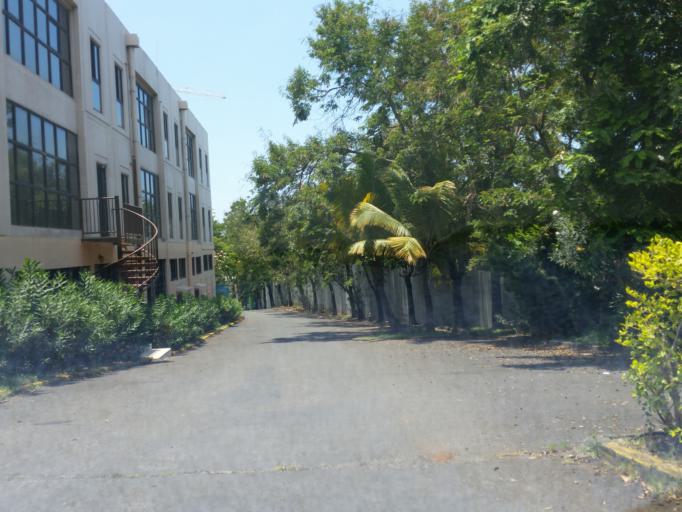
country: RE
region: Reunion
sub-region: Reunion
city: Saint-Denis
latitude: -20.8954
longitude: 55.4741
